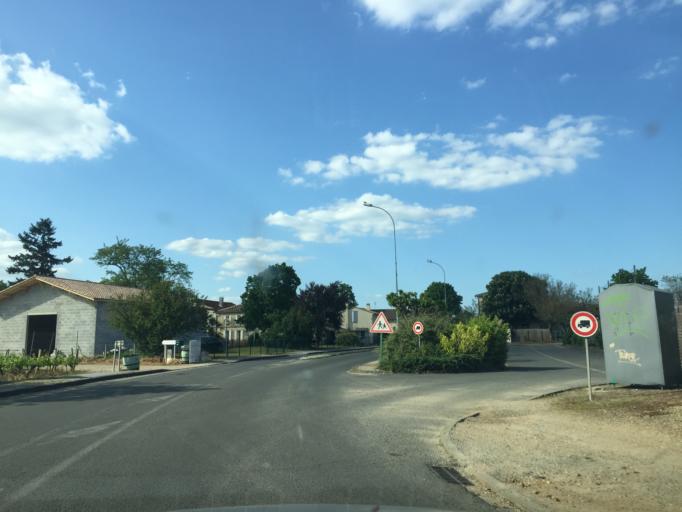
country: FR
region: Aquitaine
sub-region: Departement de la Gironde
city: Libourne
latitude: 44.9546
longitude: -0.2080
